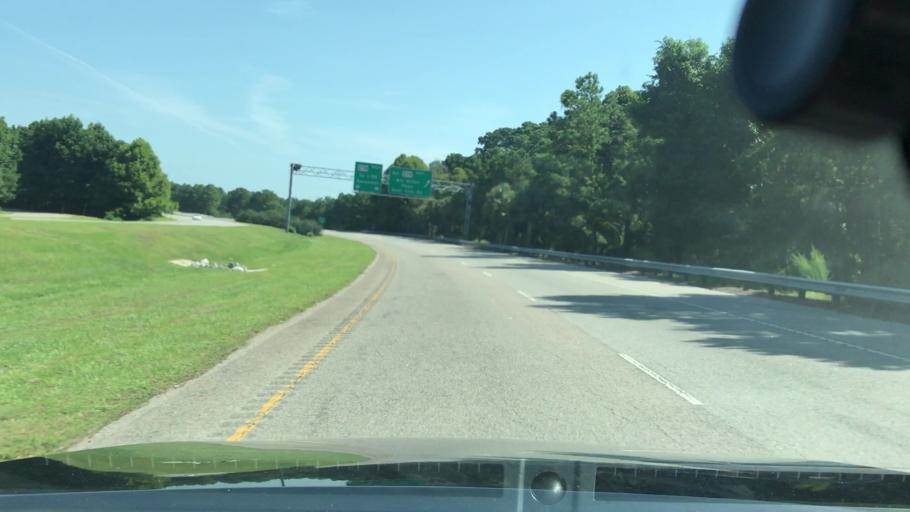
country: US
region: South Carolina
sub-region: Beaufort County
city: Hilton Head Island
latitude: 32.2098
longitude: -80.7392
